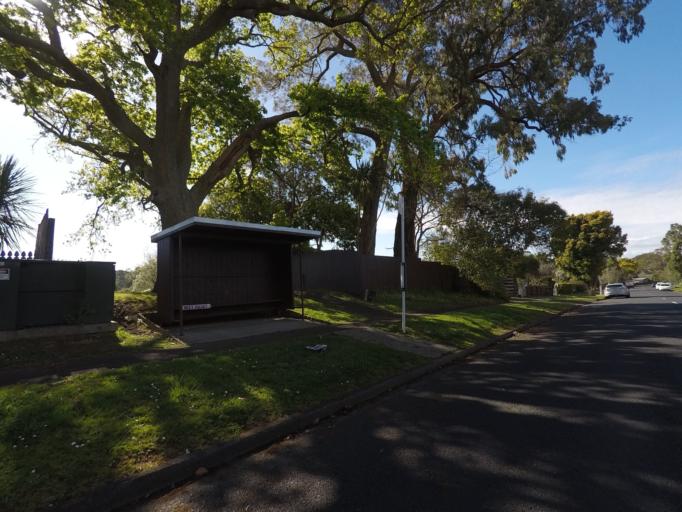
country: NZ
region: Auckland
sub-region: Auckland
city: Rosebank
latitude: -36.8622
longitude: 174.5985
